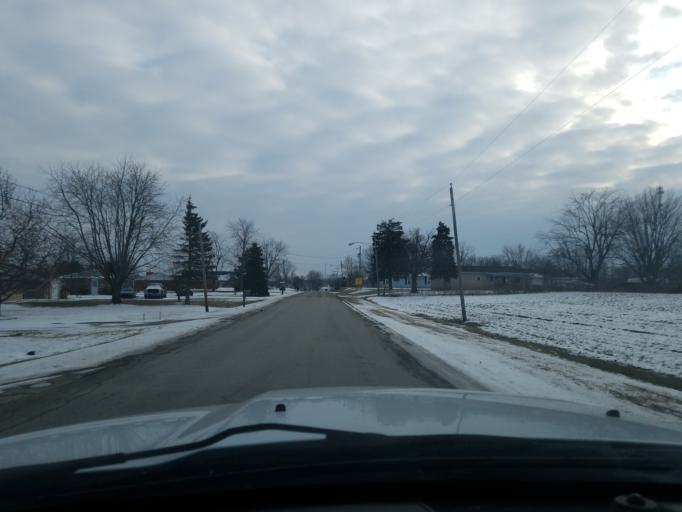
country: US
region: Indiana
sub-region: Randolph County
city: Winchester
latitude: 40.1927
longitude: -84.9806
